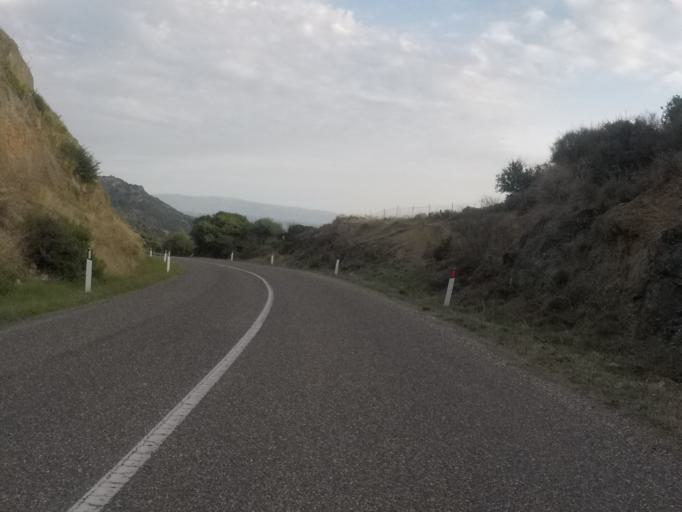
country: IT
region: Sardinia
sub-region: Provincia di Oristano
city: Montresta
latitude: 40.3651
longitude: 8.4105
